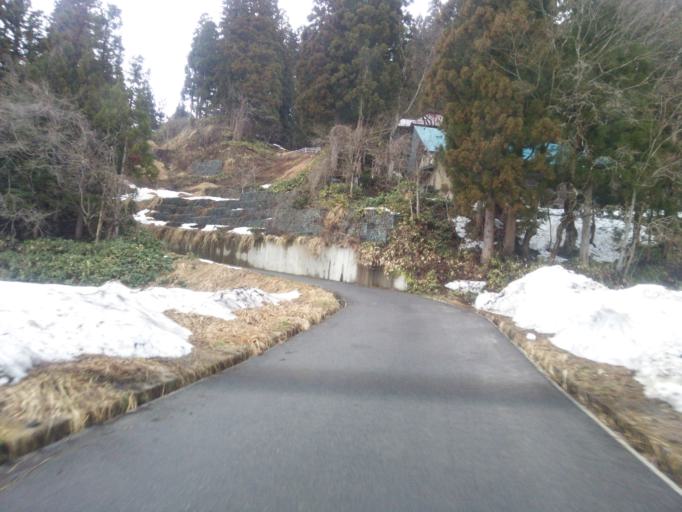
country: JP
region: Fukushima
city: Kitakata
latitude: 37.6884
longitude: 139.9467
